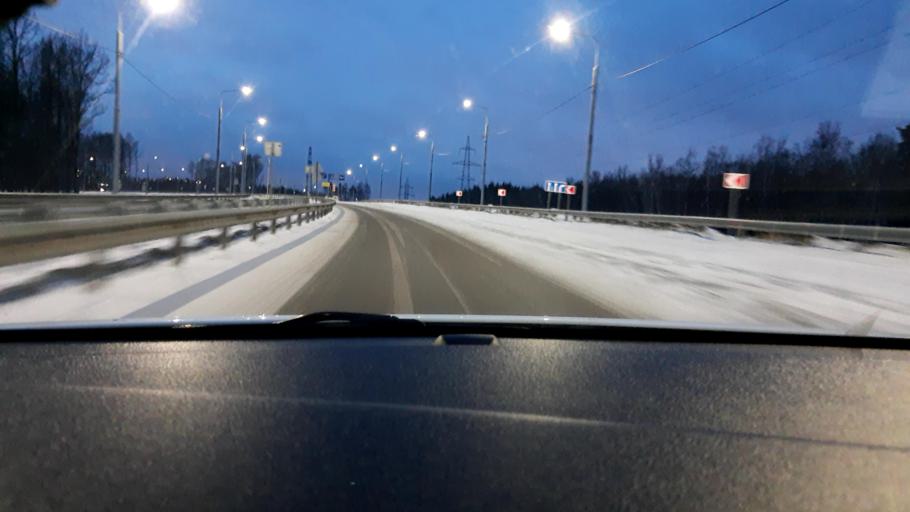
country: RU
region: Moskovskaya
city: Barvikha
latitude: 55.7157
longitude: 37.3119
